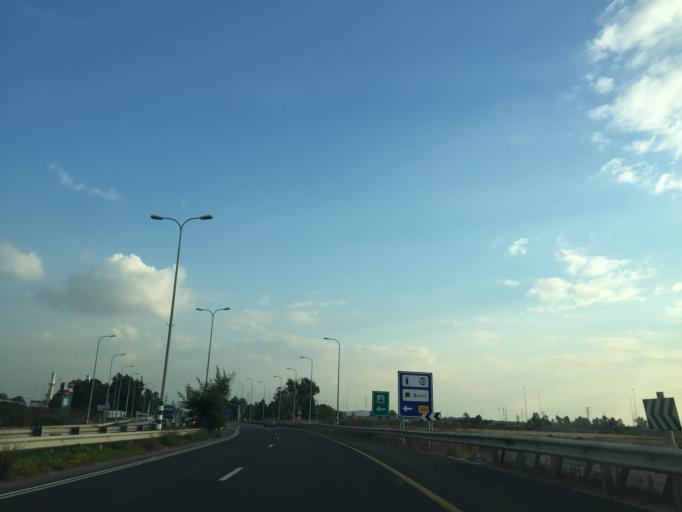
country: IL
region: Central District
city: Ramla
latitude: 31.9183
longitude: 34.8858
